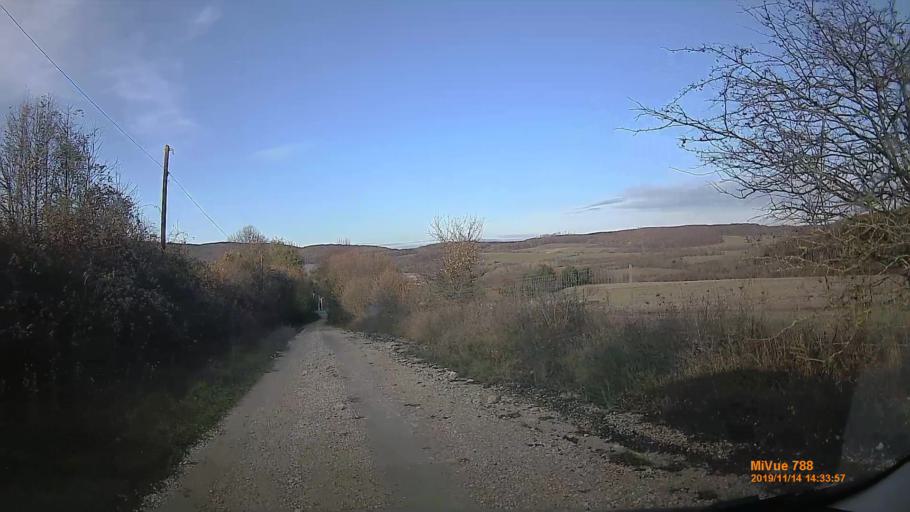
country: HU
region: Veszprem
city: Zirc
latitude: 47.2207
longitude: 17.7896
